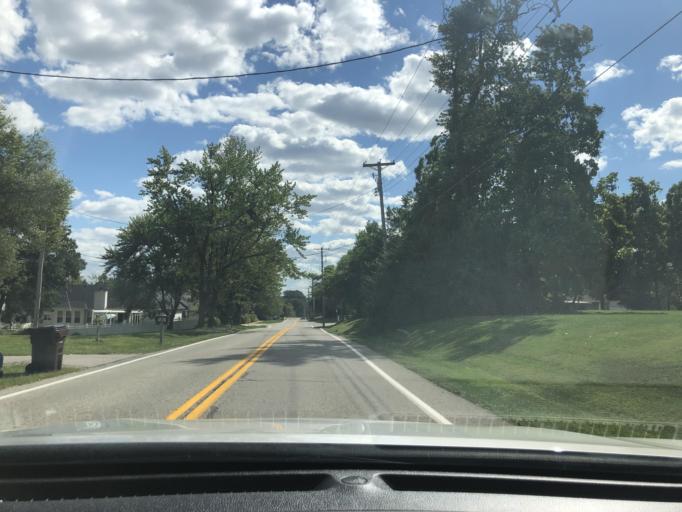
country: US
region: Missouri
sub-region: Saint Louis County
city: Green Park
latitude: 38.5130
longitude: -90.3429
